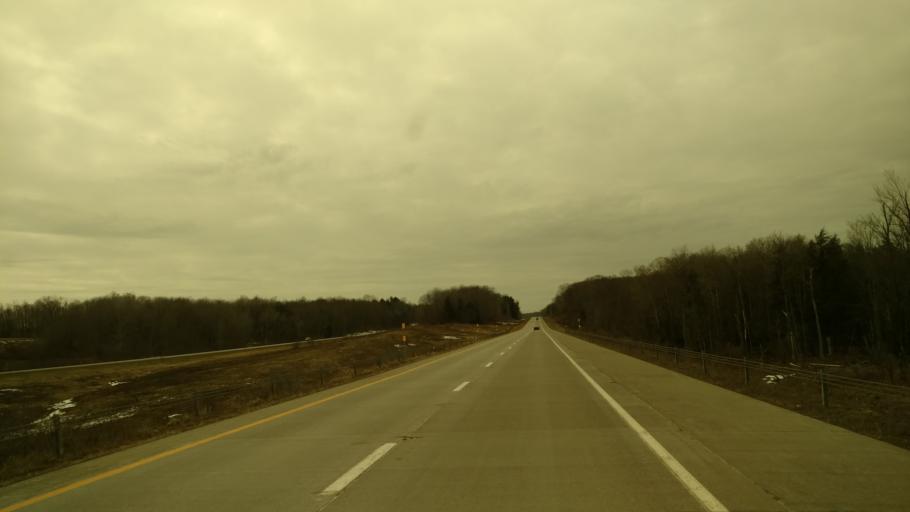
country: US
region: New York
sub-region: Chautauqua County
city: Mayville
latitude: 42.1548
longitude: -79.4507
